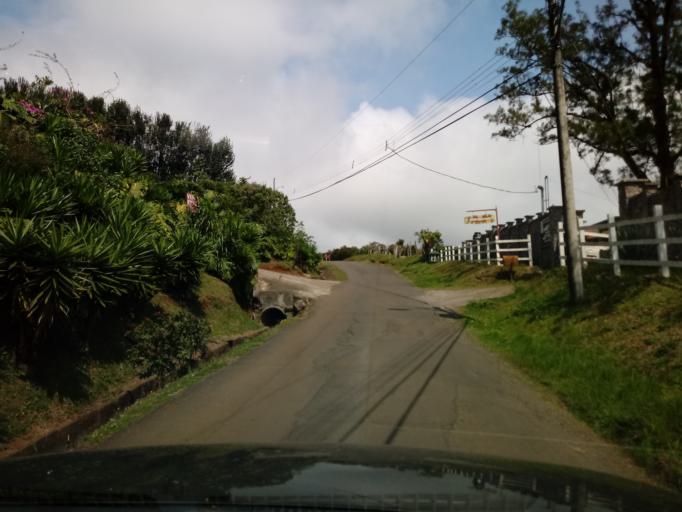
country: CR
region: Heredia
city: Angeles
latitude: 10.0295
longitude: -84.0341
